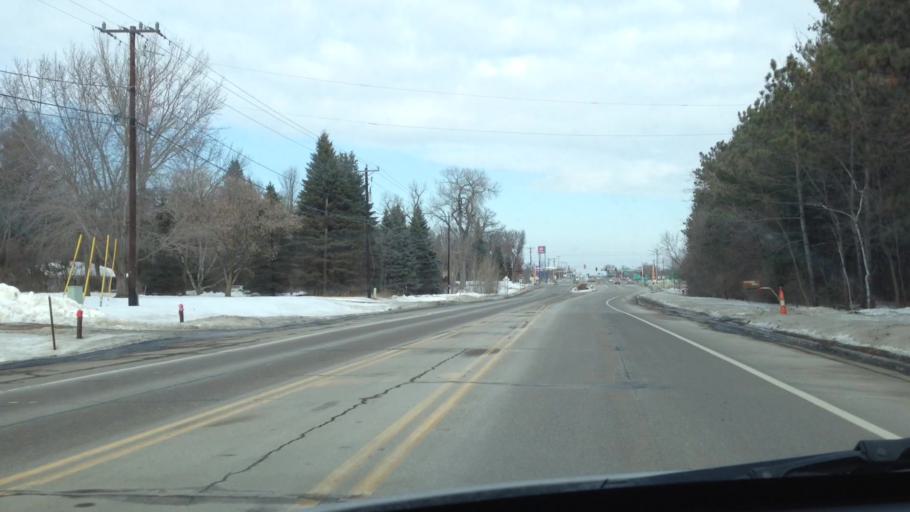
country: US
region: Minnesota
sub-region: Anoka County
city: Lino Lakes
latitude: 45.1746
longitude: -93.1167
